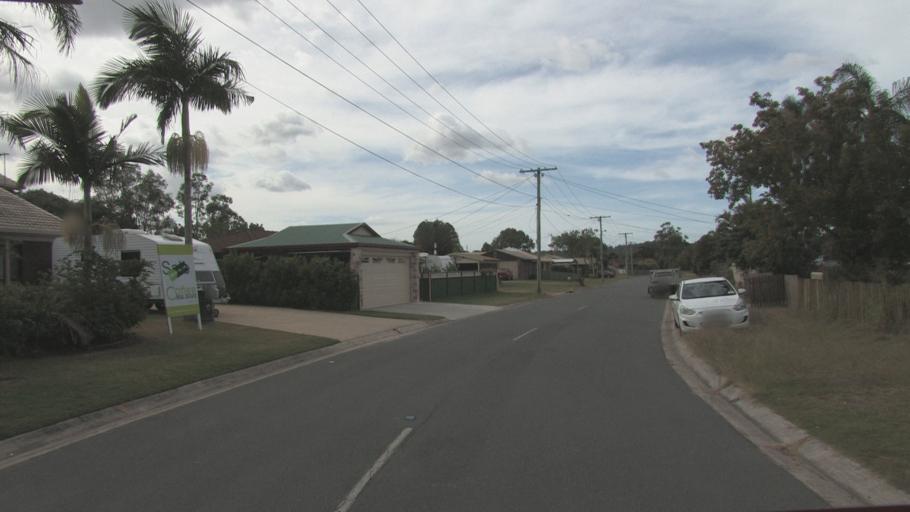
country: AU
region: Queensland
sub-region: Logan
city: Waterford West
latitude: -27.6802
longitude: 153.1504
